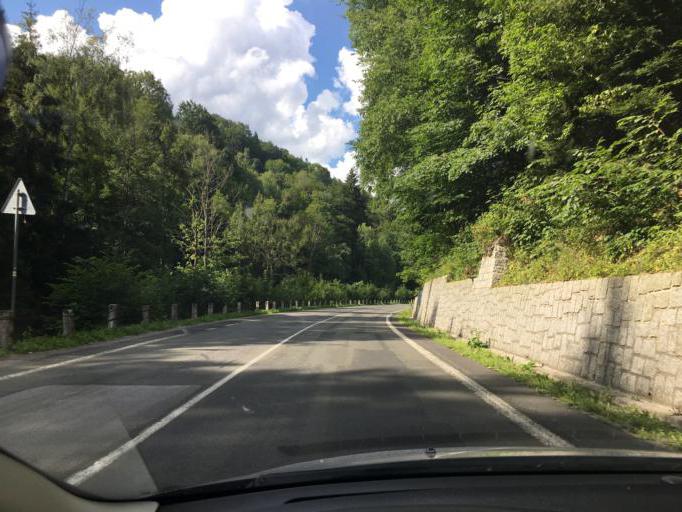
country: CZ
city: Benecko
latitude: 50.6854
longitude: 15.5778
